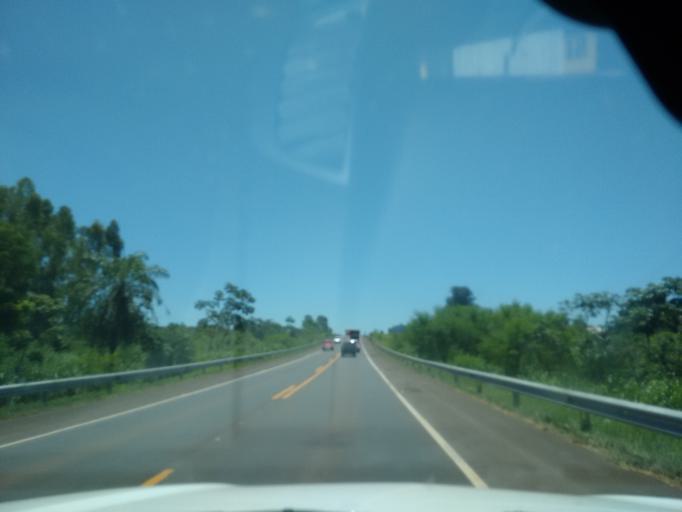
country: PY
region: Canindeyu
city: Salto del Guaira
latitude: -24.0193
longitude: -54.2952
